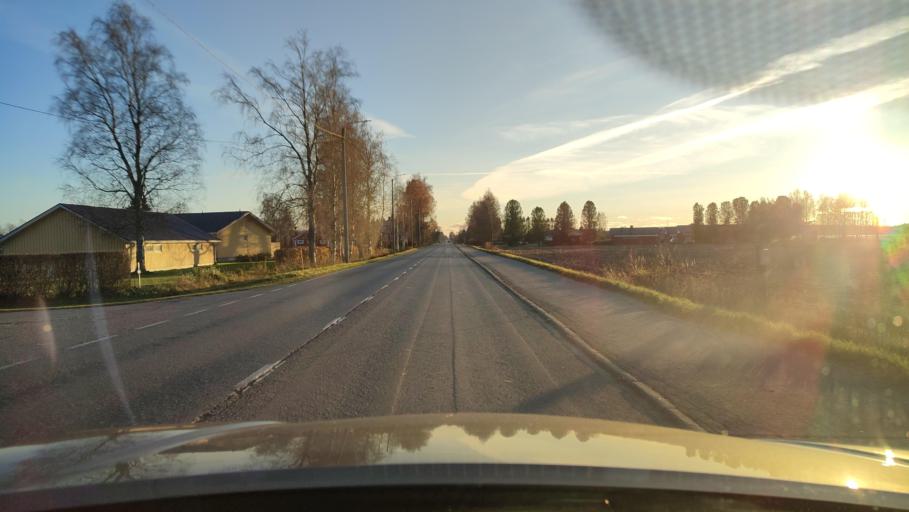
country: FI
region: Ostrobothnia
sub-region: Sydosterbotten
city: Naerpes
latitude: 62.5426
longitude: 21.3940
